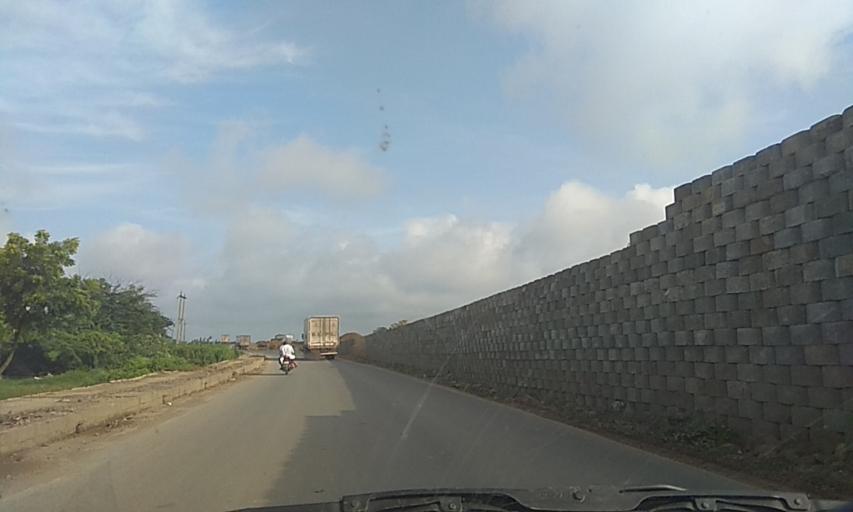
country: IN
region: Karnataka
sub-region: Haveri
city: Savanur
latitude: 14.8718
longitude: 75.3182
